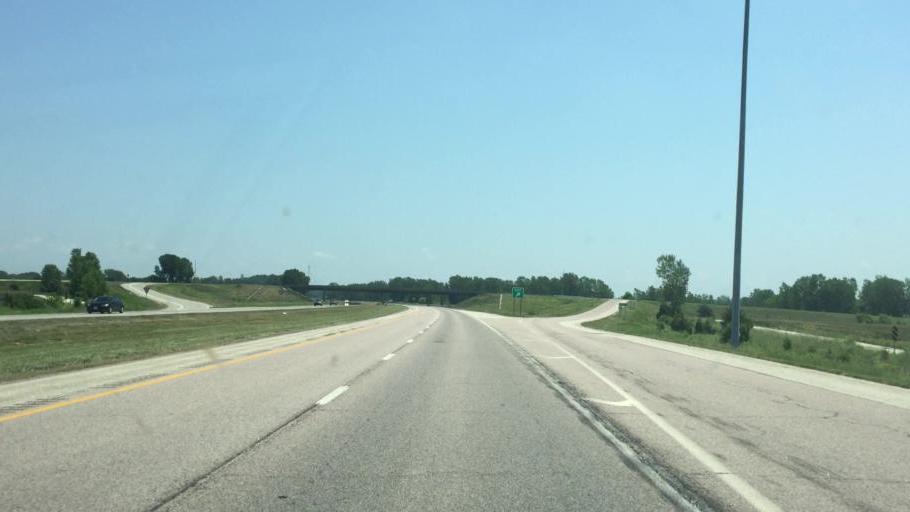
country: US
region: Kansas
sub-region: Doniphan County
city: Elwood
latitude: 39.7404
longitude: -94.8986
